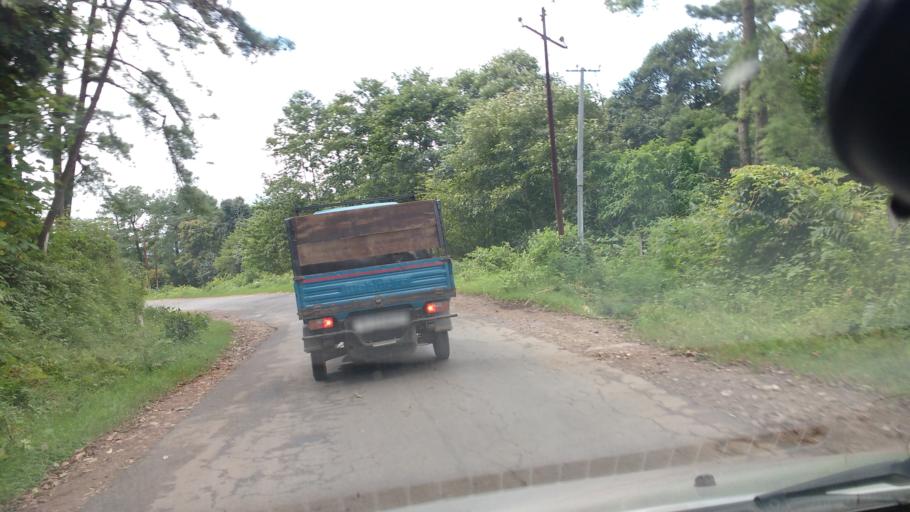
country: IN
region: Meghalaya
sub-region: East Khasi Hills
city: Shillong
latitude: 25.5482
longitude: 91.8438
